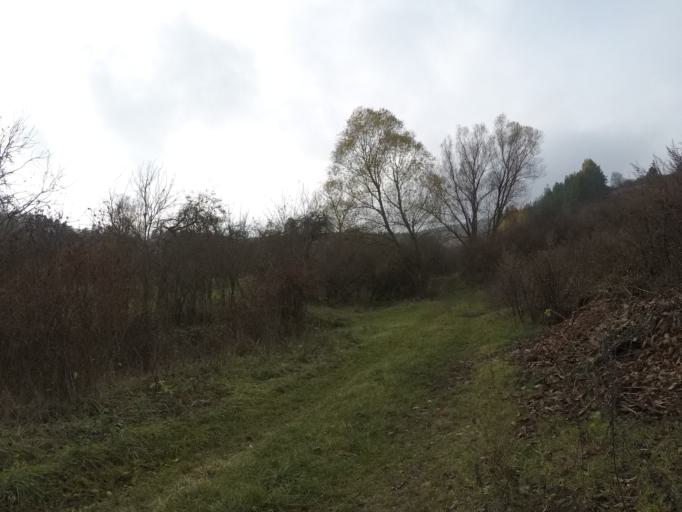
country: SK
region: Presovsky
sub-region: Okres Presov
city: Presov
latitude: 48.9004
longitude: 21.1842
